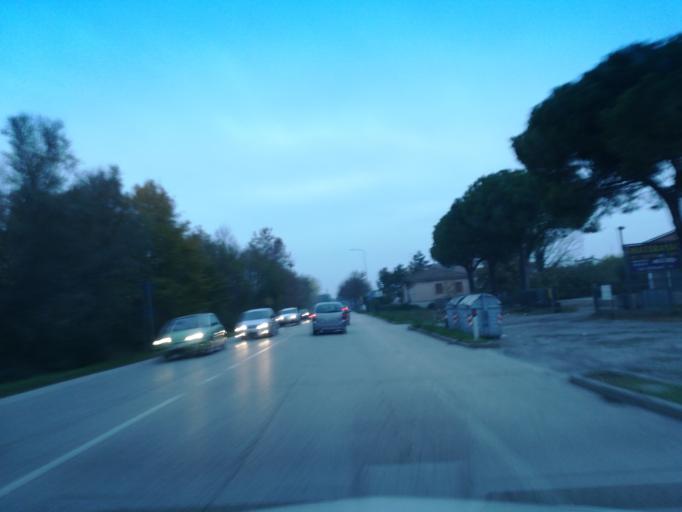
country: IT
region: Emilia-Romagna
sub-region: Provincia di Ravenna
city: Faenza
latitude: 44.3015
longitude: 11.8919
